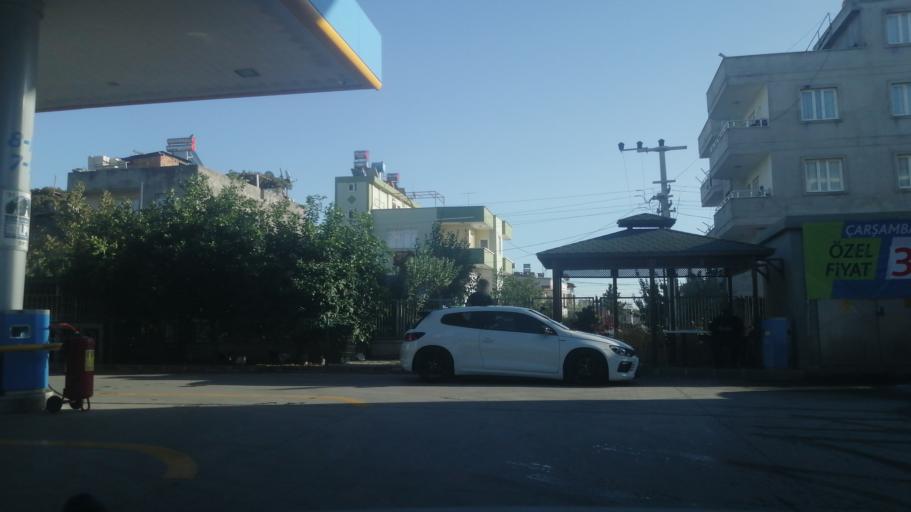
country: TR
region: Adana
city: Seyhan
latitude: 37.0208
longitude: 35.2742
